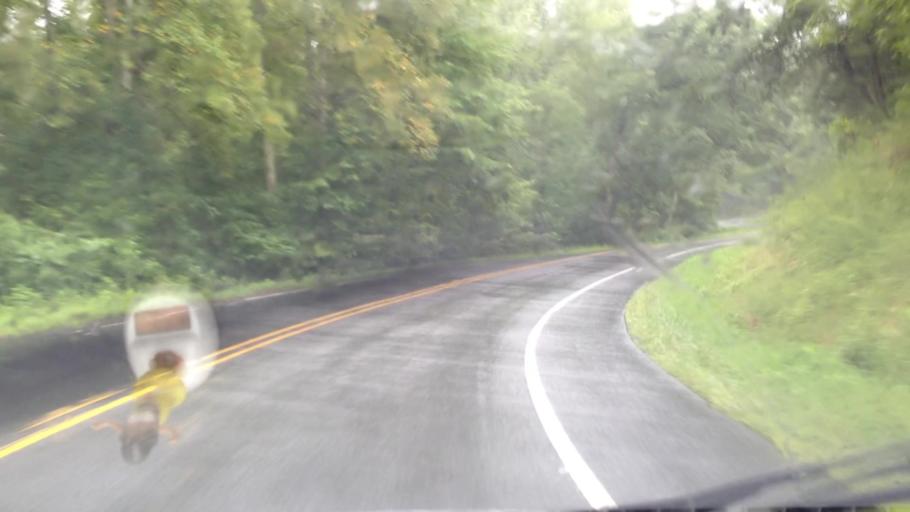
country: US
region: North Carolina
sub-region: Stokes County
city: Walnut Cove
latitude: 36.3145
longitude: -80.0434
